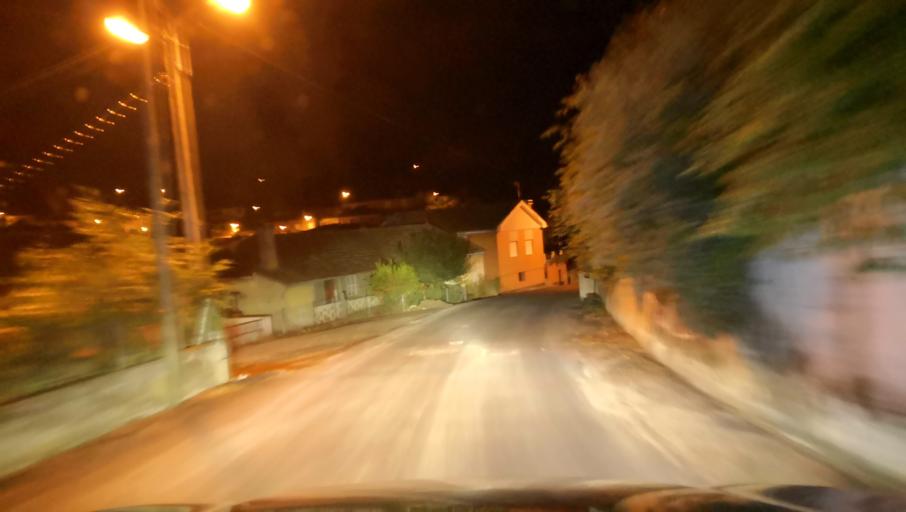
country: PT
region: Vila Real
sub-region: Sabrosa
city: Vilela
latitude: 41.2071
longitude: -7.6937
